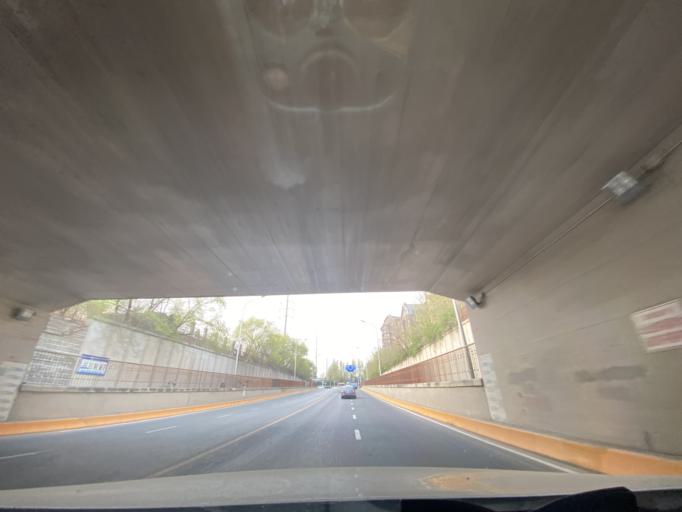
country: CN
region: Beijing
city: Babaoshan
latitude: 39.9309
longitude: 116.2326
